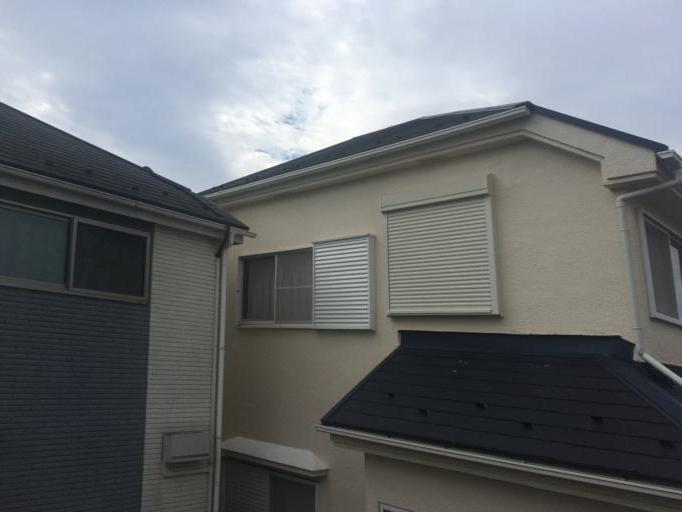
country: JP
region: Tokyo
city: Hino
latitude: 35.7023
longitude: 139.3615
